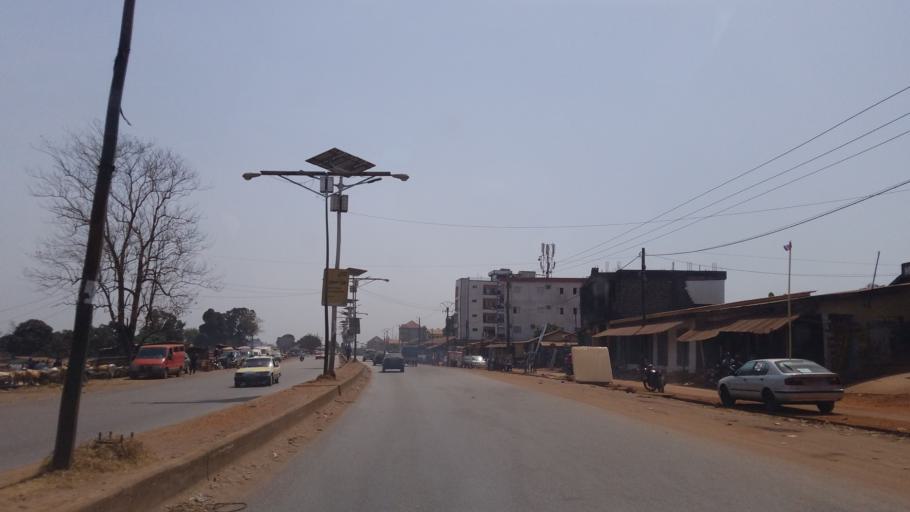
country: GN
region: Conakry
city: Conakry
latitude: 9.6151
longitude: -13.6069
